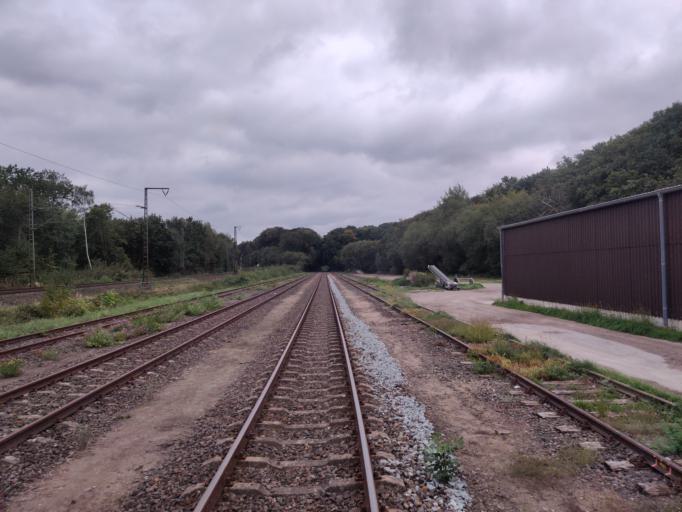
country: DE
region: Lower Saxony
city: Osterholz-Scharmbeck
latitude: 53.2274
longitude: 8.8018
